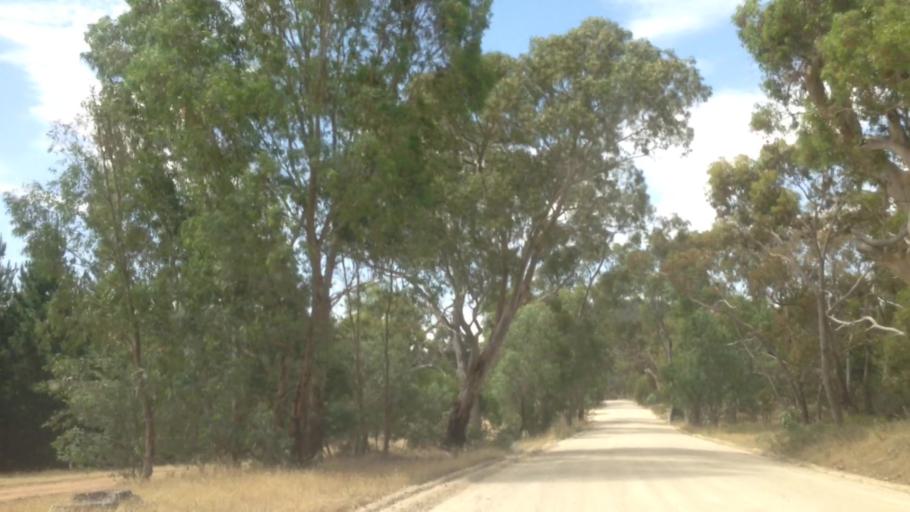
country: AU
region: South Australia
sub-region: Barossa
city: Williamstown
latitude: -34.7094
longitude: 138.9592
